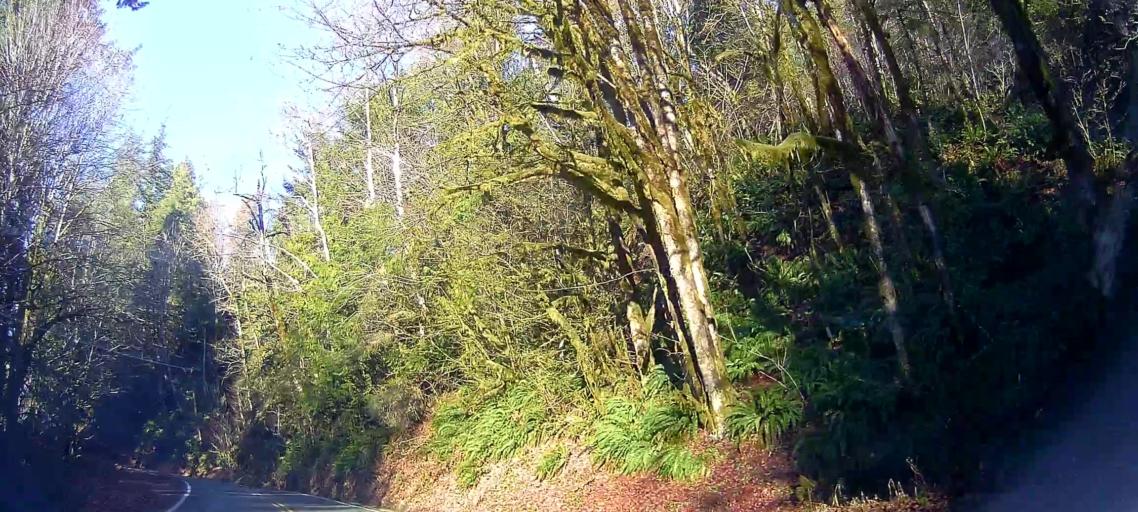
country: US
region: Washington
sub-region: Snohomish County
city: Darrington
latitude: 48.5487
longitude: -121.7658
